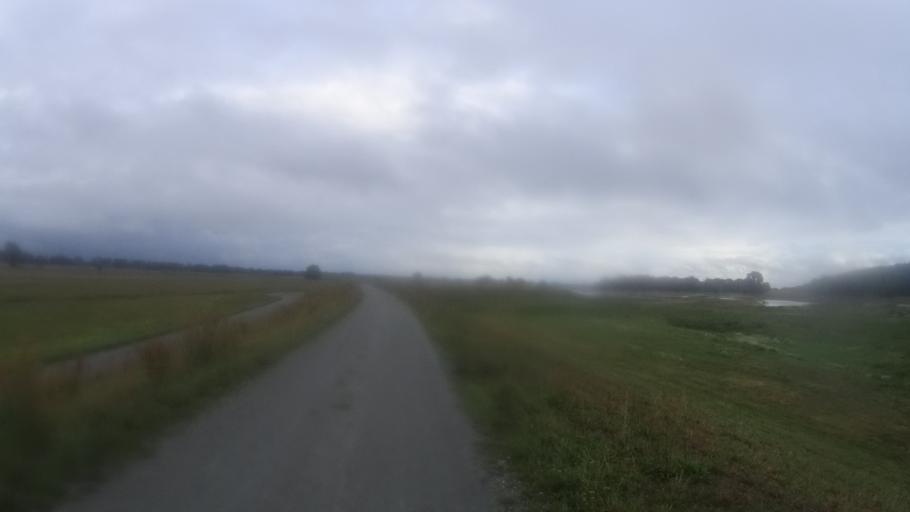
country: DE
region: Brandenburg
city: Lenzen
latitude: 53.0792
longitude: 11.4309
